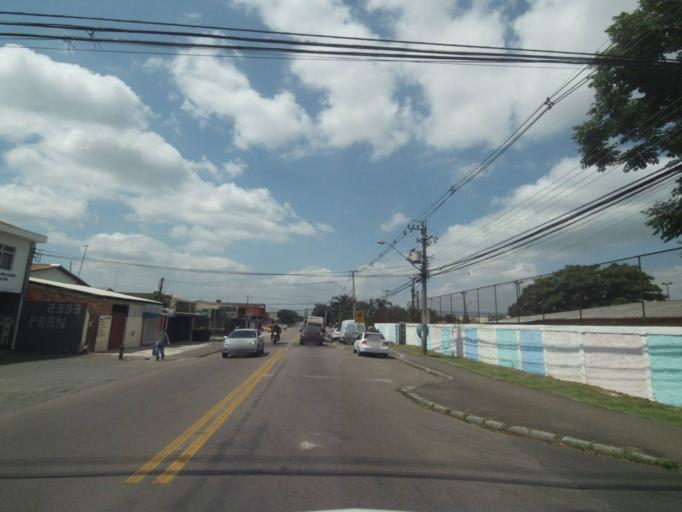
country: BR
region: Parana
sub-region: Sao Jose Dos Pinhais
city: Sao Jose dos Pinhais
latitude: -25.5332
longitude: -49.2581
